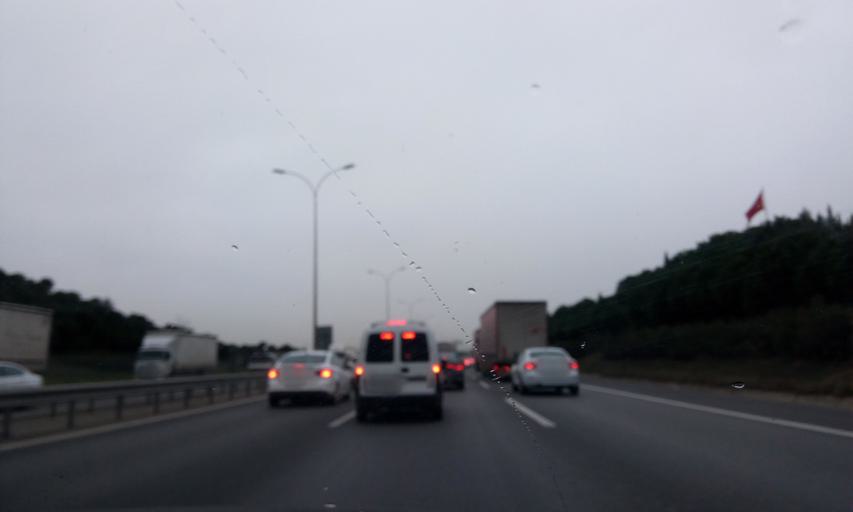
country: TR
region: Kocaeli
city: Balcik
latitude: 40.8601
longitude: 29.4040
